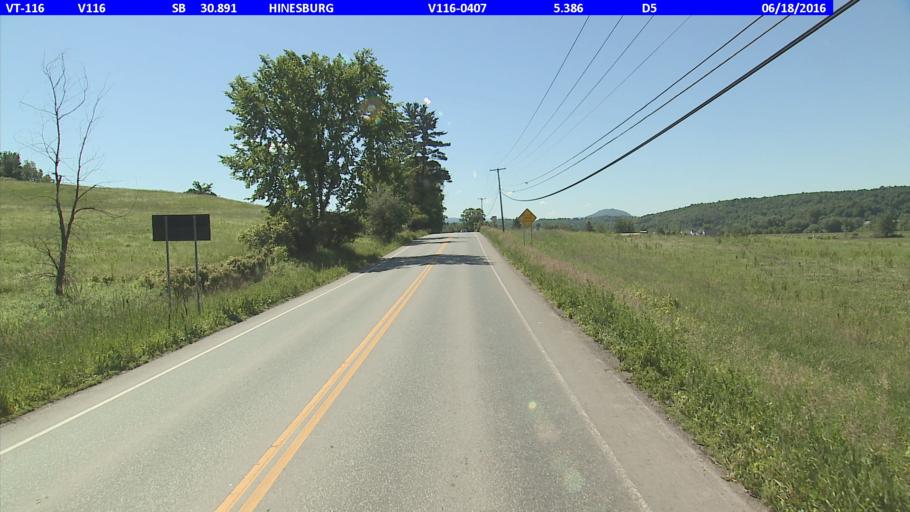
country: US
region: Vermont
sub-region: Chittenden County
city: Hinesburg
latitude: 44.3403
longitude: -73.1159
